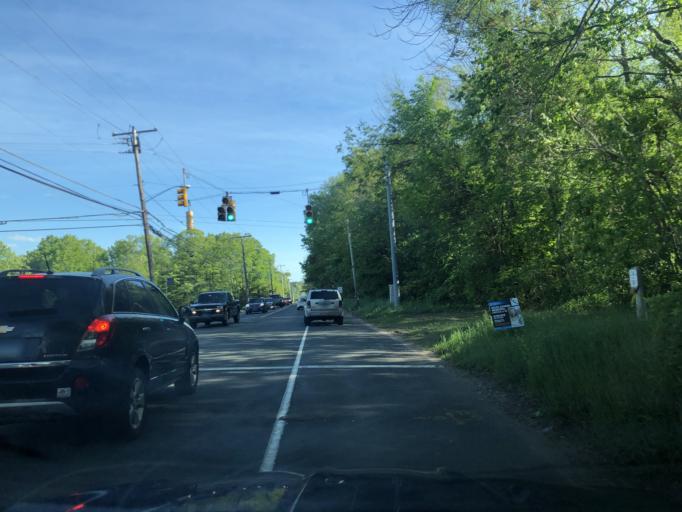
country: US
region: Connecticut
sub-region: Hartford County
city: Canton Valley
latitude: 41.7997
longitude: -72.8614
